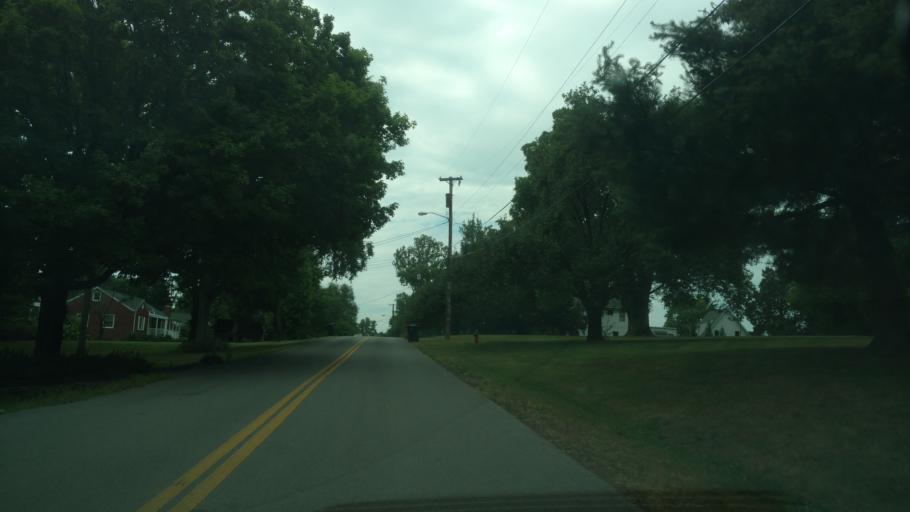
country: US
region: Tennessee
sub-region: Davidson County
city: Lakewood
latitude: 36.2107
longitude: -86.7039
